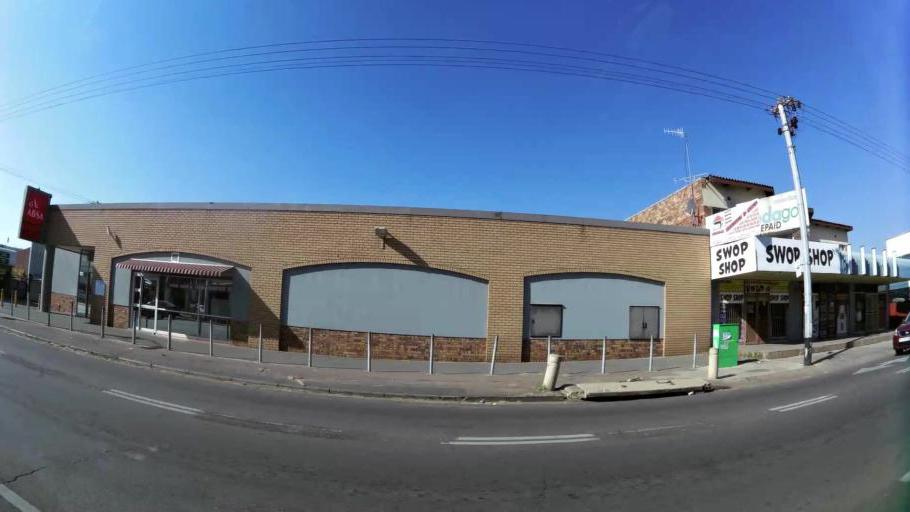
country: ZA
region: Gauteng
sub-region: City of Tshwane Metropolitan Municipality
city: Pretoria
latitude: -25.7145
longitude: 28.2019
